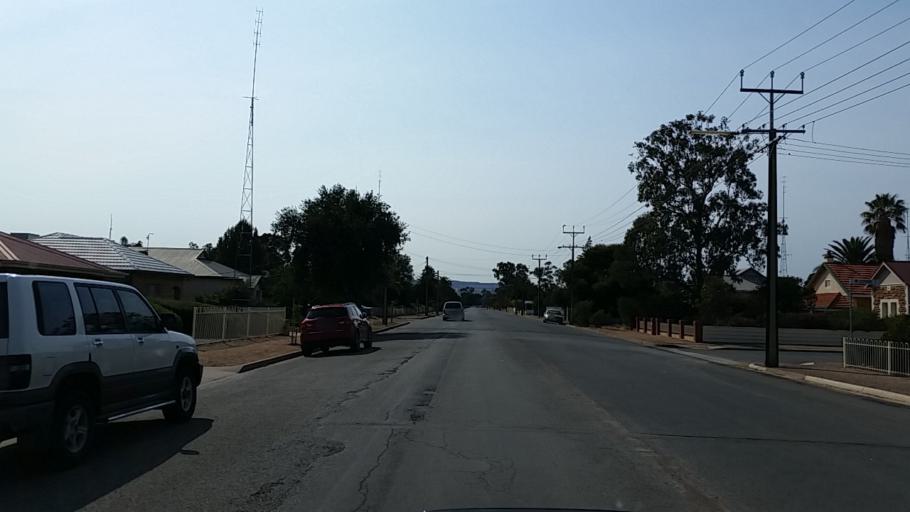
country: AU
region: South Australia
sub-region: Port Pirie City and Dists
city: Port Pirie
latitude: -33.1813
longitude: 137.9937
